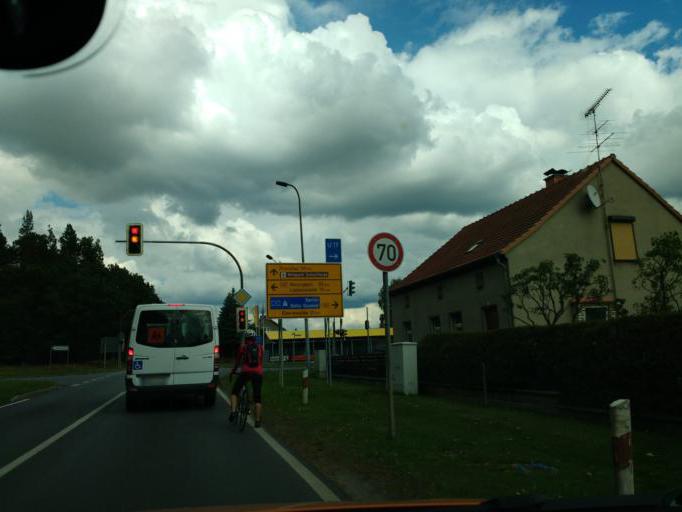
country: DE
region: Brandenburg
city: Marienwerder
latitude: 52.8582
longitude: 13.5316
